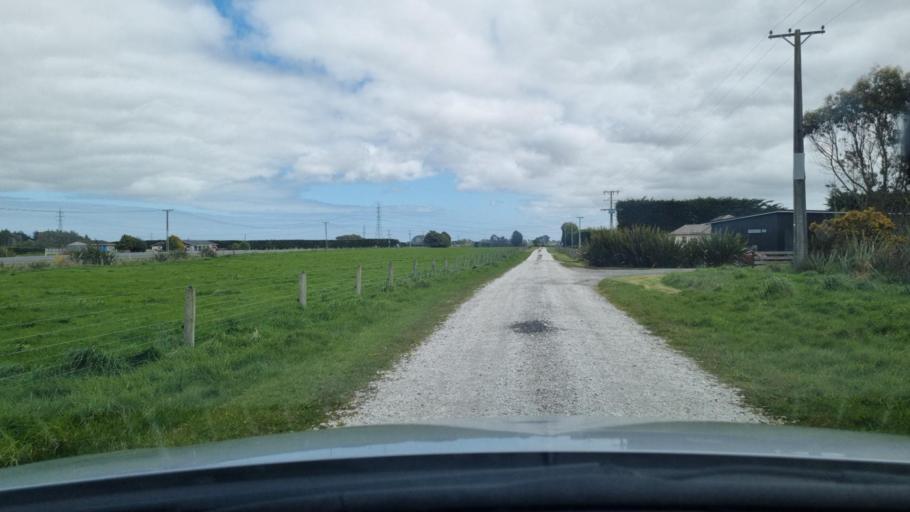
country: NZ
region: Southland
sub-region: Invercargill City
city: Invercargill
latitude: -46.4510
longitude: 168.4577
